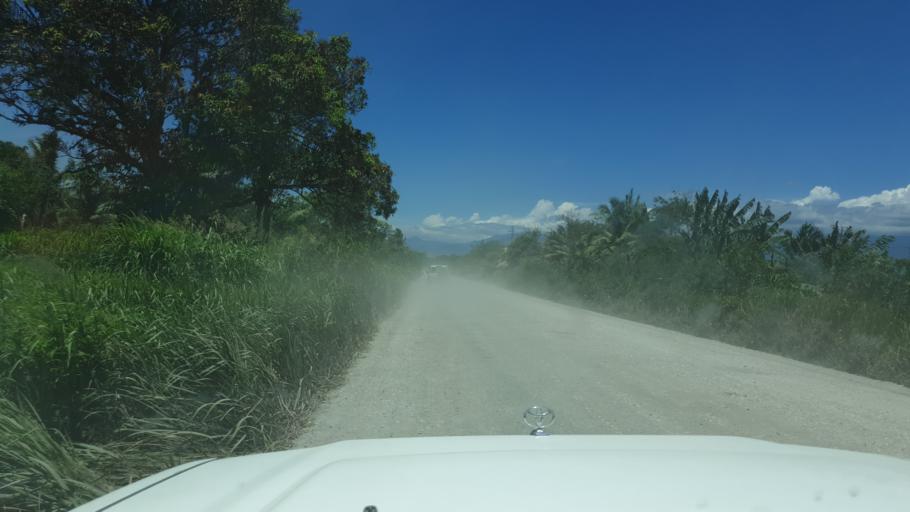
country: PG
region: Eastern Highlands
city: Goroka
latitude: -5.6763
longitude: 145.5016
